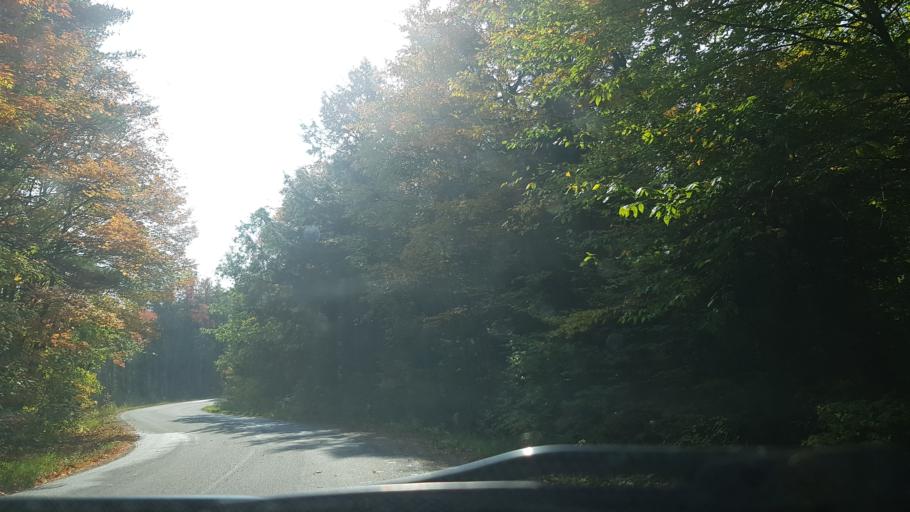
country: CA
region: Ontario
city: Bracebridge
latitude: 44.9743
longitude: -79.2594
